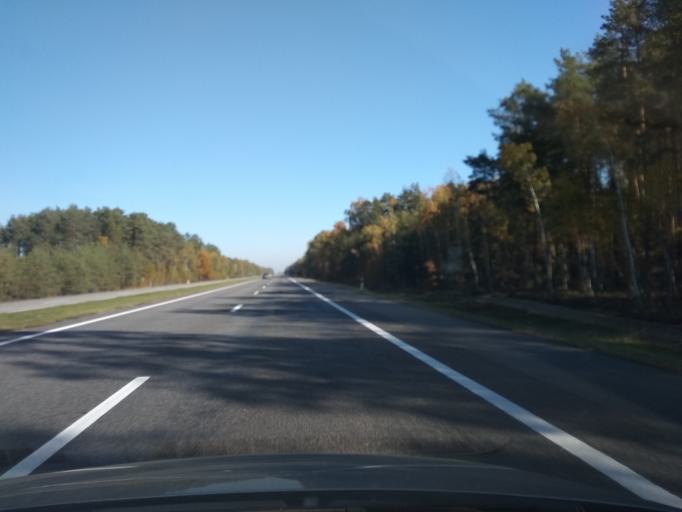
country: BY
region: Brest
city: Antopal'
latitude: 52.3704
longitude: 24.7426
